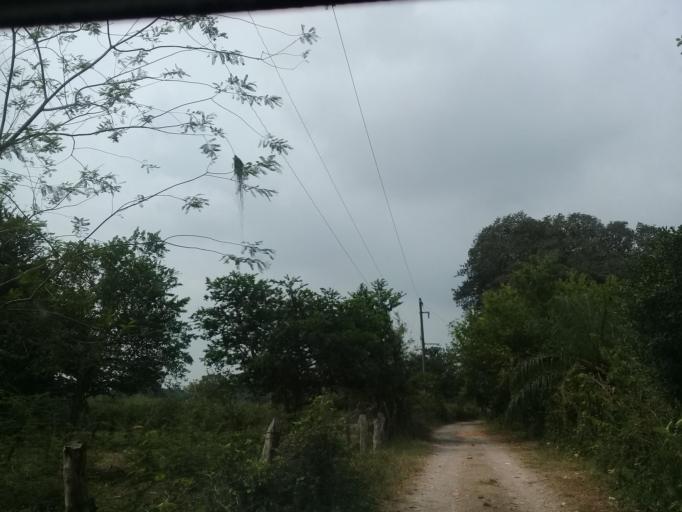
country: MX
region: Veracruz
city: El Tejar
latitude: 19.0579
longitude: -96.1916
